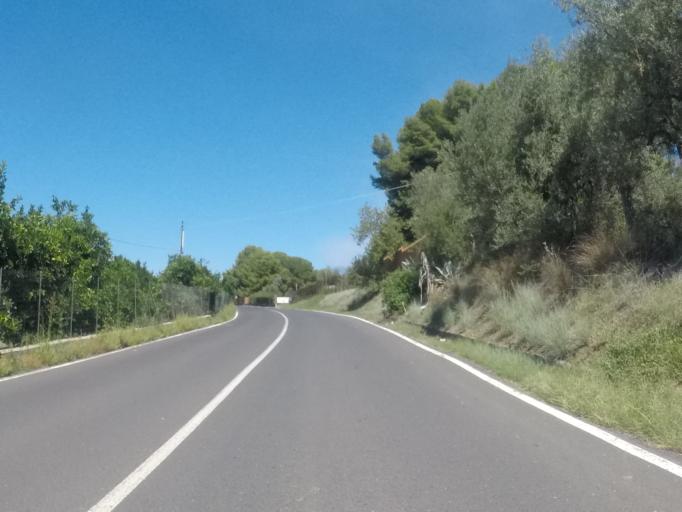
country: IT
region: Sicily
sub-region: Catania
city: Motta Sant'Anastasia
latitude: 37.4814
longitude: 14.9447
